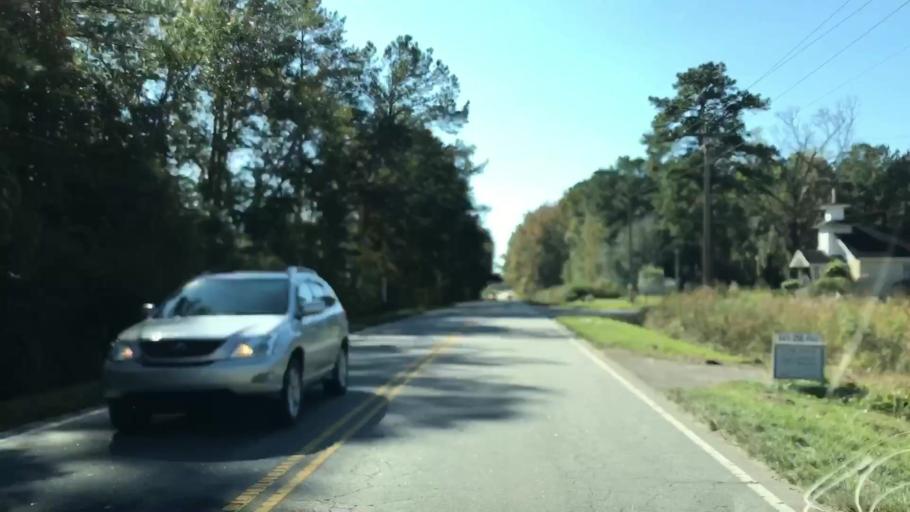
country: US
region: South Carolina
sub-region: Jasper County
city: Ridgeland
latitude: 32.4281
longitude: -80.8964
